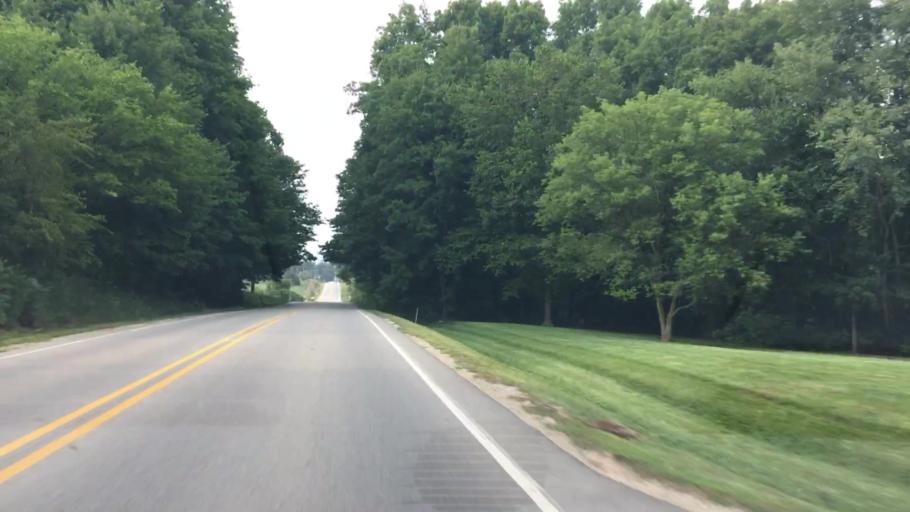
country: US
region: Michigan
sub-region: Ottawa County
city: Hudsonville
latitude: 42.8414
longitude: -85.9006
